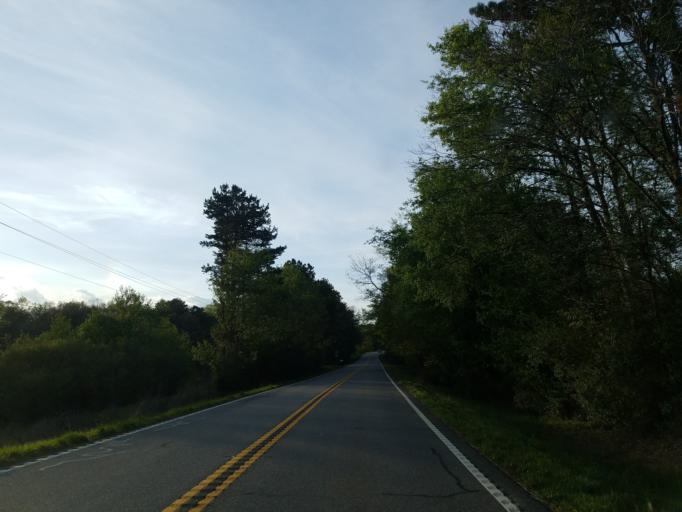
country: US
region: Georgia
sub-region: Fannin County
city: Blue Ridge
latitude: 34.8476
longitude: -84.2173
